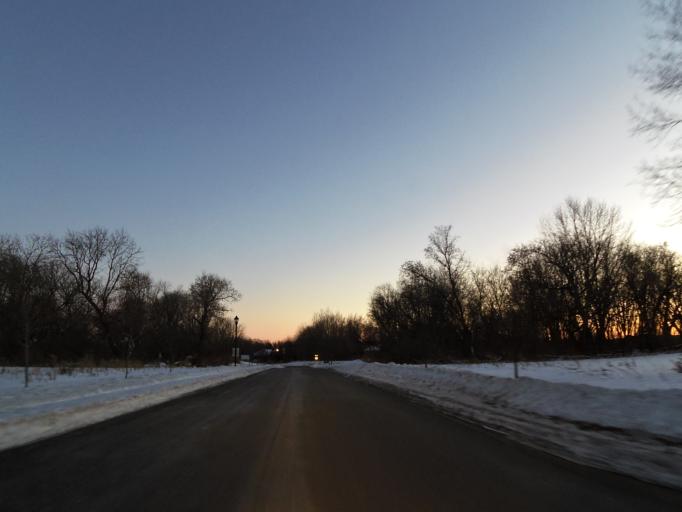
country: US
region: Minnesota
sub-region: Washington County
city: Lake Elmo
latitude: 45.0070
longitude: -92.8781
